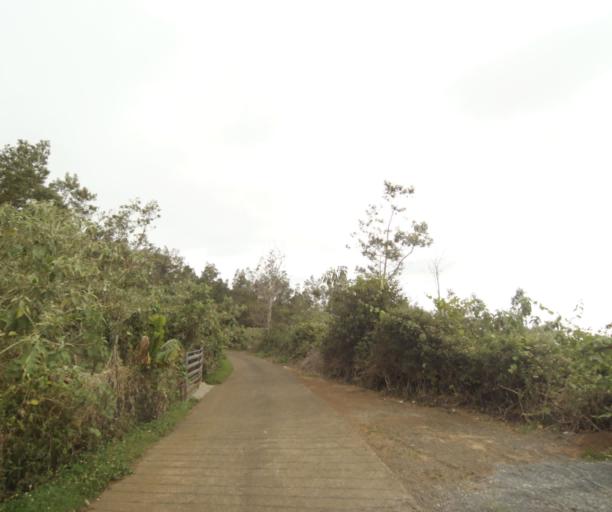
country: RE
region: Reunion
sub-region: Reunion
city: Saint-Paul
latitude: -21.0136
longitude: 55.3521
